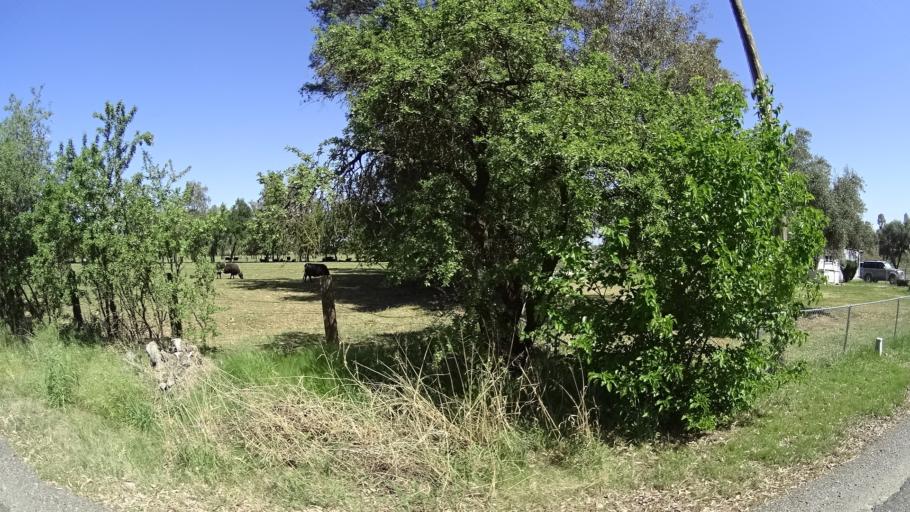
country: US
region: California
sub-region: Glenn County
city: Orland
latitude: 39.7870
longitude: -122.1573
